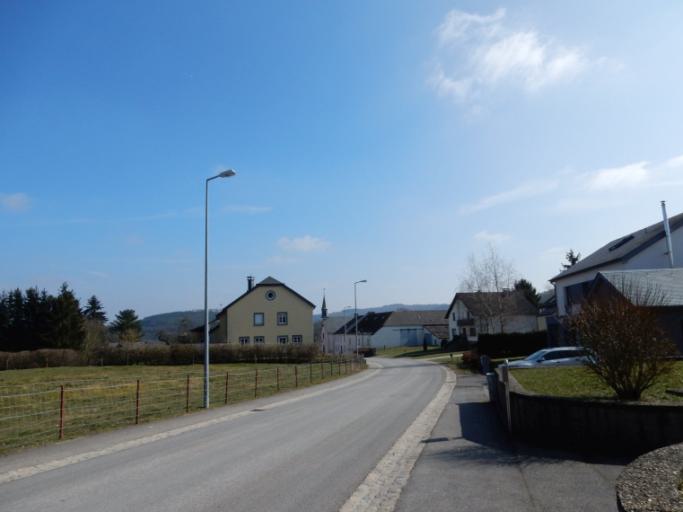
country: LU
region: Diekirch
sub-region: Canton de Wiltz
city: Winseler
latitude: 49.9674
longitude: 5.8868
